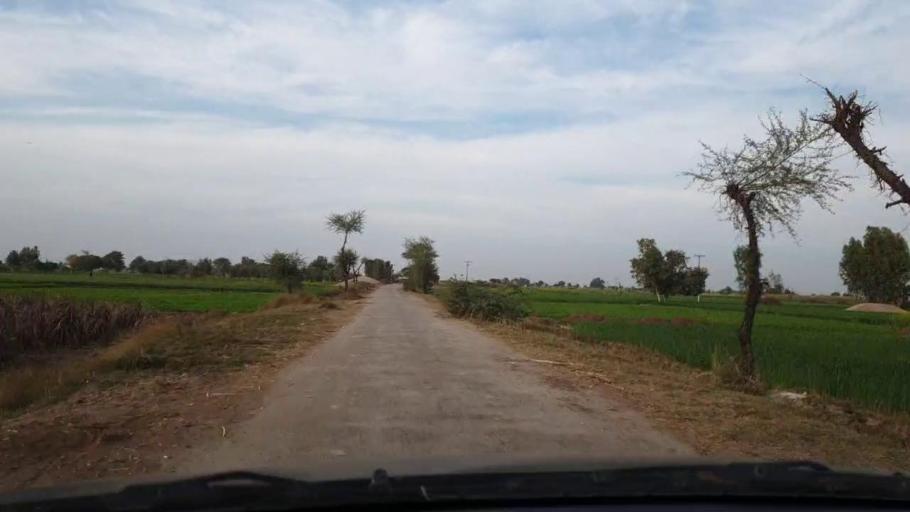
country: PK
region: Sindh
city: Khadro
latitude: 26.1640
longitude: 68.7263
